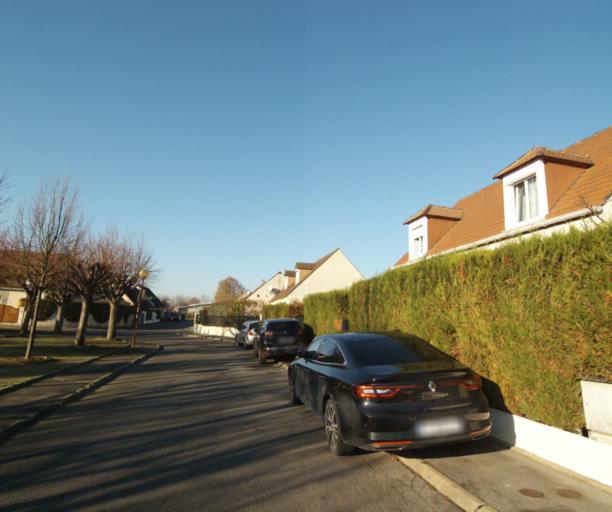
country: FR
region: Ile-de-France
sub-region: Departement du Val-d'Oise
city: Arnouville
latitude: 48.9945
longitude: 2.4296
